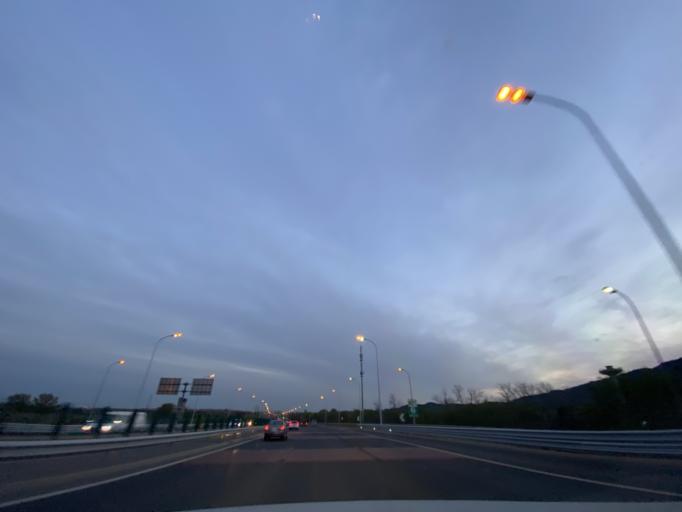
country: CN
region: Beijing
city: Xiangshan
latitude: 39.9889
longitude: 116.2152
